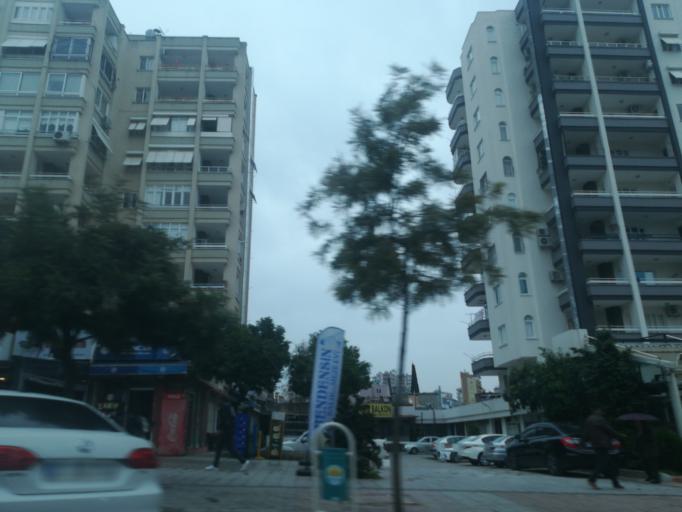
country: TR
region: Adana
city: Adana
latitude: 37.0336
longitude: 35.3085
